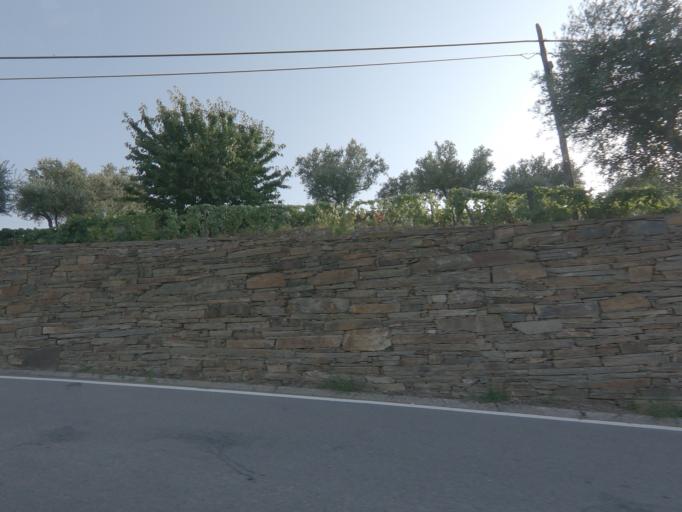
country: PT
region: Viseu
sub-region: Tabuaco
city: Tabuaco
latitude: 41.1397
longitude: -7.6024
